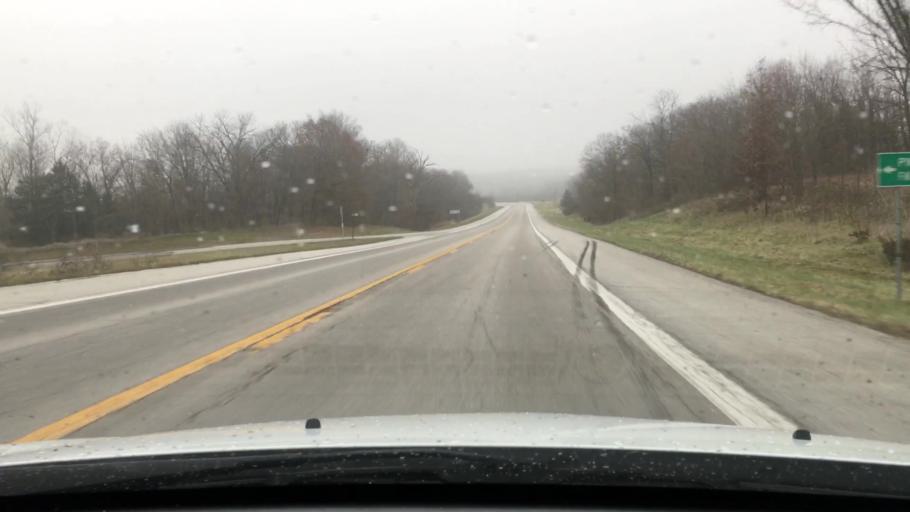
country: US
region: Missouri
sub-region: Pike County
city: Bowling Green
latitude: 39.3635
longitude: -91.1922
